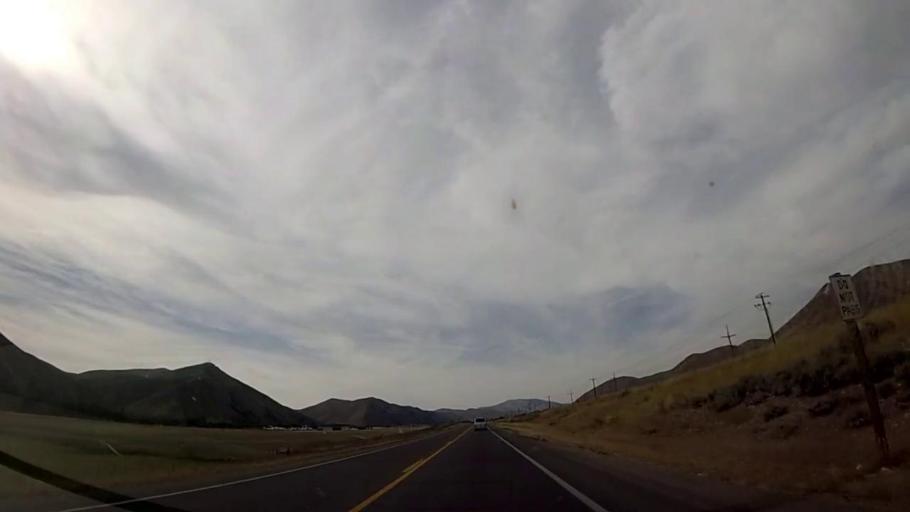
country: US
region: Idaho
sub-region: Blaine County
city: Bellevue
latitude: 43.4941
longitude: -114.2845
